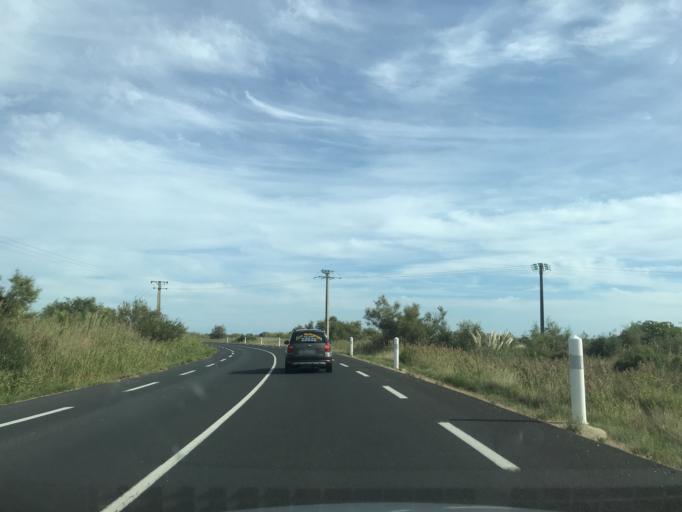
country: FR
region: Languedoc-Roussillon
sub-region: Departement du Gard
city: Aigues-Mortes
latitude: 43.5563
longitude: 4.3211
